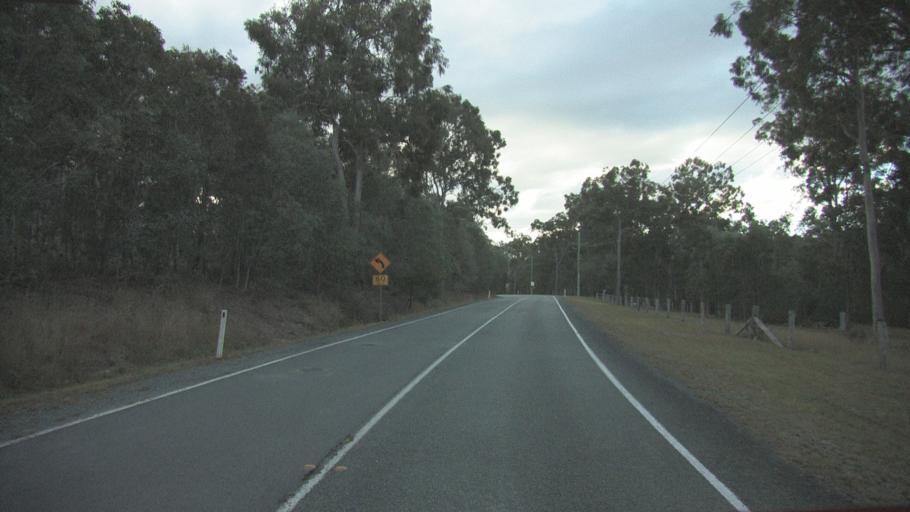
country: AU
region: Queensland
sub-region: Logan
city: Windaroo
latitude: -27.8091
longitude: 153.1541
